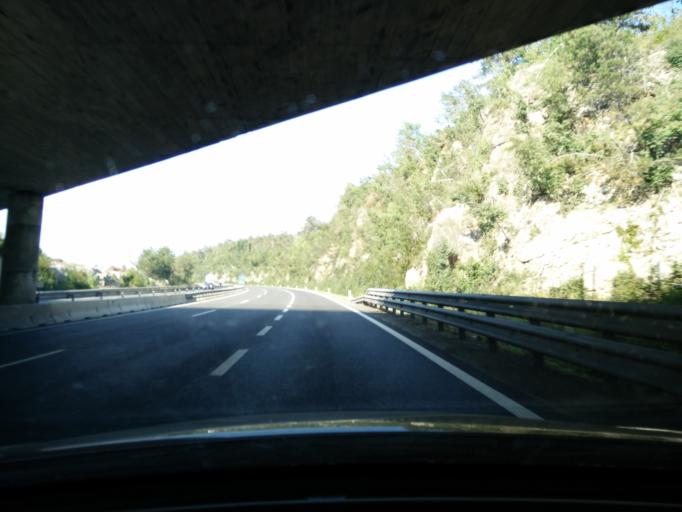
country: SI
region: Postojna
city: Postojna
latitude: 45.7695
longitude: 14.2216
